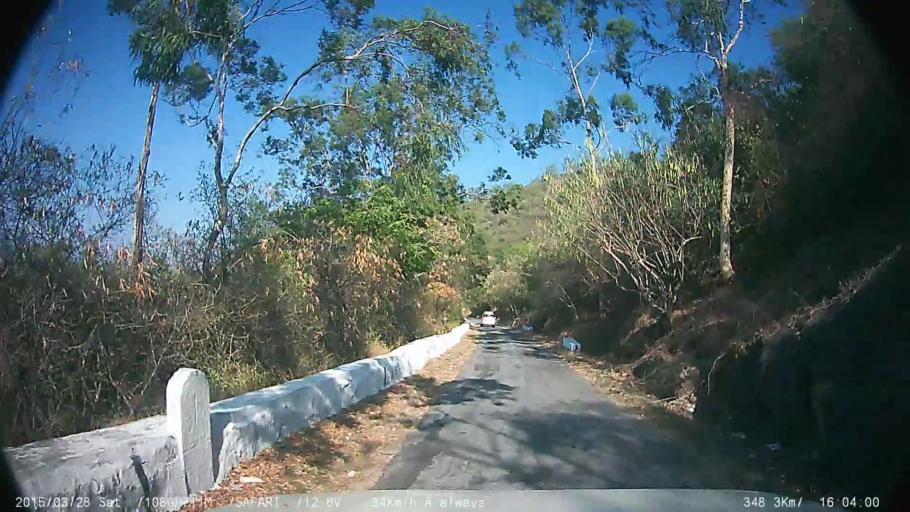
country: IN
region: Karnataka
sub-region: Mysore
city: Mysore
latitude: 12.2813
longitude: 76.6730
